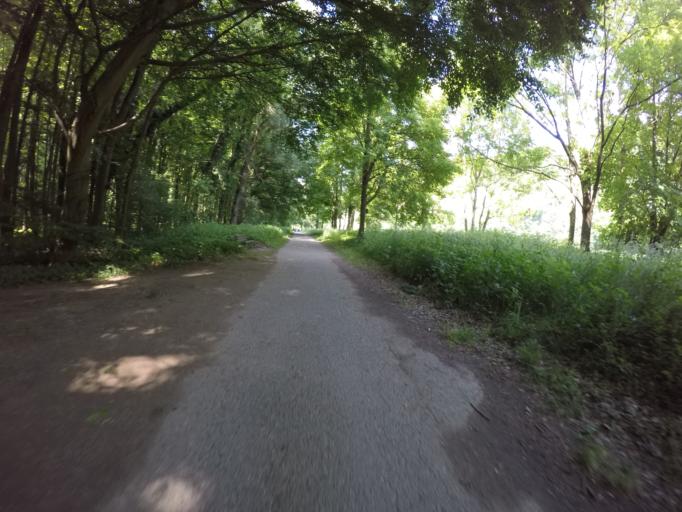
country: DE
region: Bavaria
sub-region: Lower Bavaria
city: Ihrlerstein
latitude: 48.9075
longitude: 11.8501
